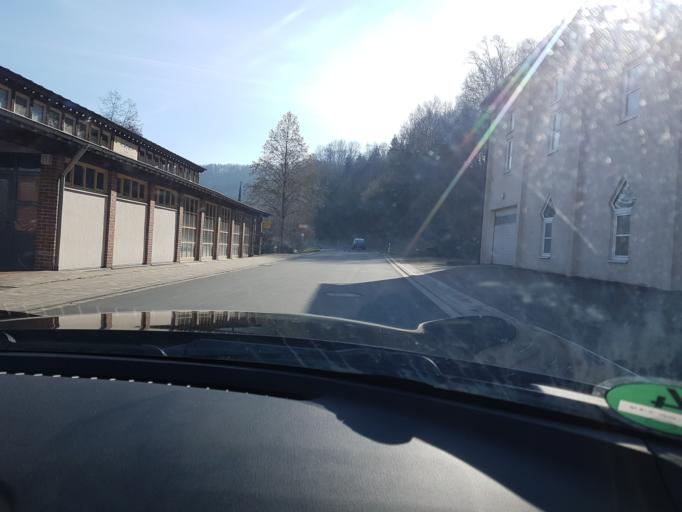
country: DE
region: Baden-Wuerttemberg
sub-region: Regierungsbezirk Stuttgart
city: Mulfingen
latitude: 49.3066
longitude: 9.8027
